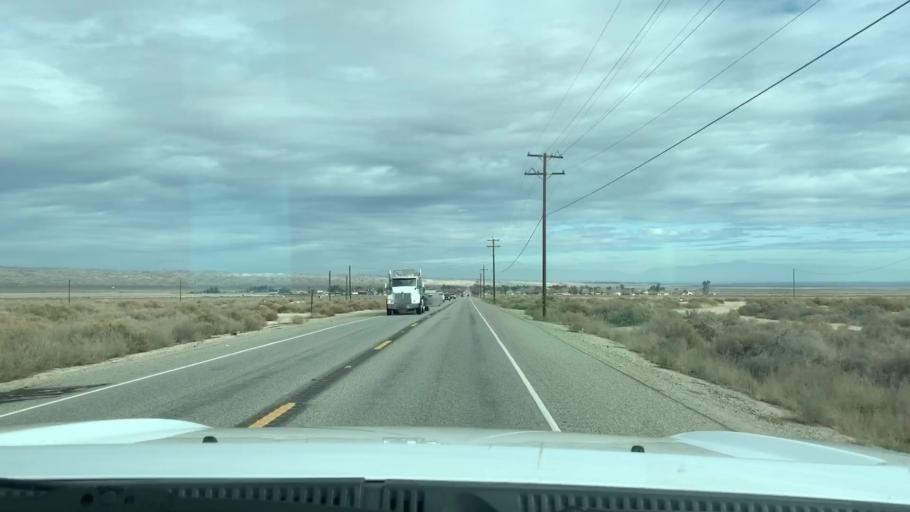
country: US
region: California
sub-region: Kern County
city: Ford City
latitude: 35.1970
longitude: -119.4240
